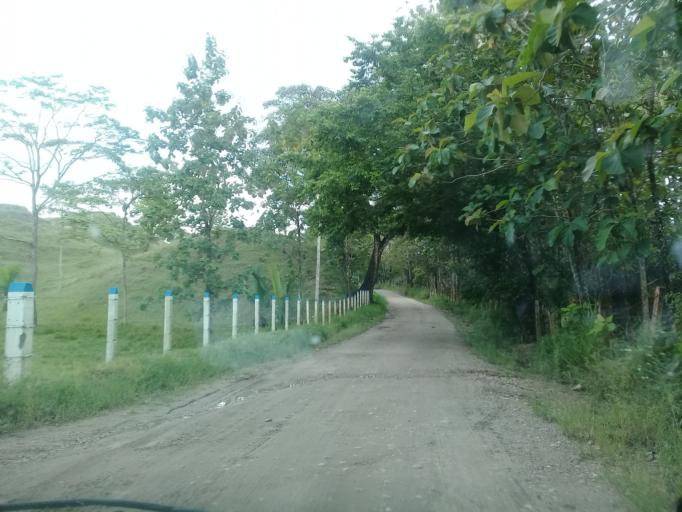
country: CO
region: Antioquia
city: Puerto Triunfo
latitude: 5.7146
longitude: -74.5833
